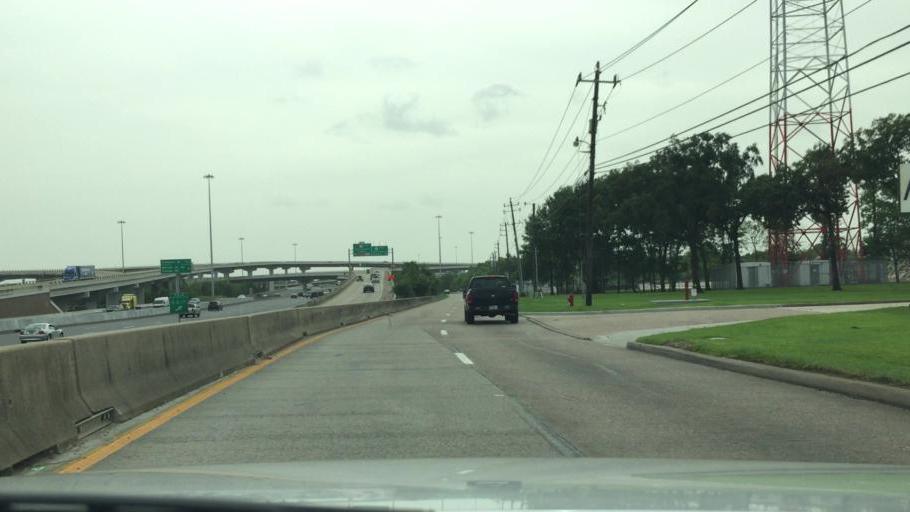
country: US
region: Texas
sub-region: Harris County
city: Cloverleaf
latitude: 29.7733
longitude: -95.1465
